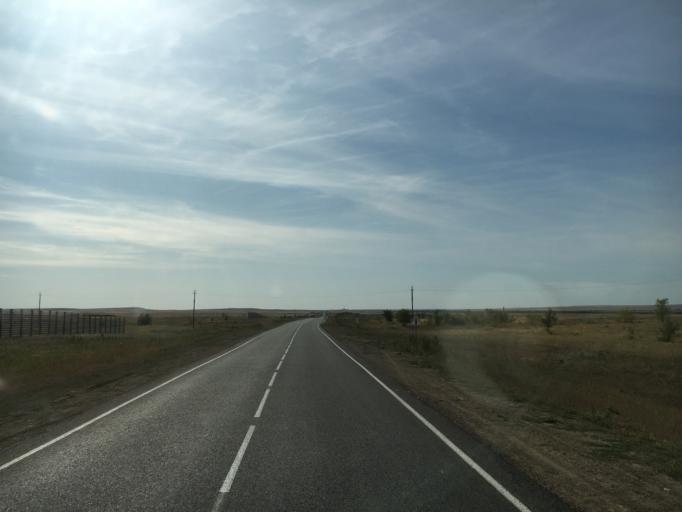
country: KZ
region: Batys Qazaqstan
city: Kamenka
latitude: 51.1086
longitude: 50.4417
